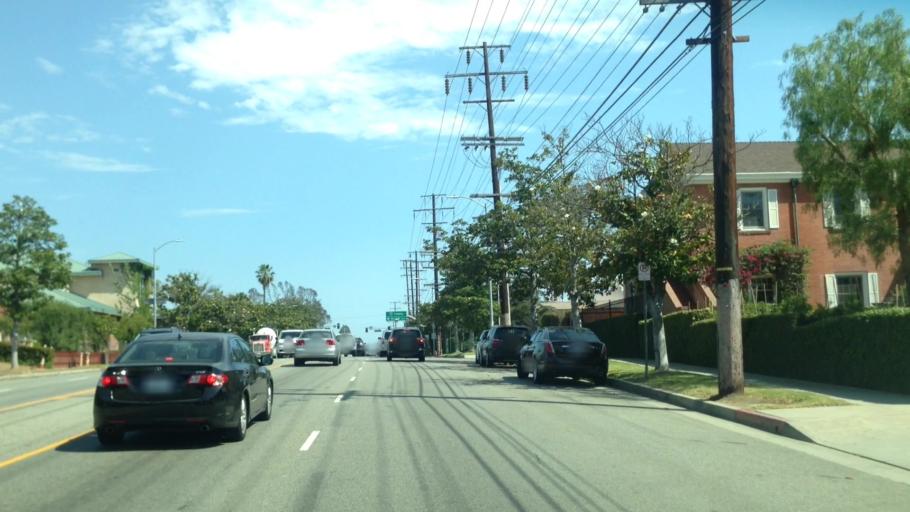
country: US
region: California
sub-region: Los Angeles County
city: Century City
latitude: 34.0344
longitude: -118.4192
